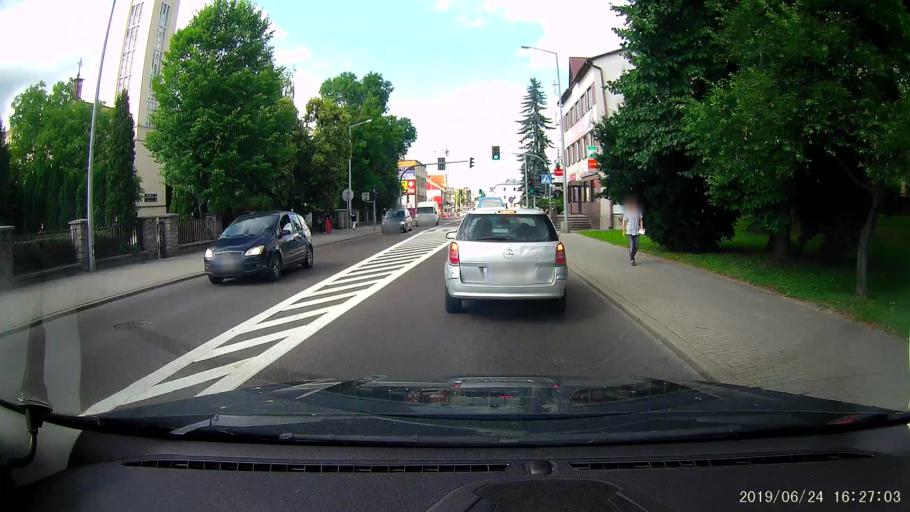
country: PL
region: Lublin Voivodeship
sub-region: Powiat tomaszowski
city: Tomaszow Lubelski
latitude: 50.4493
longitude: 23.4172
